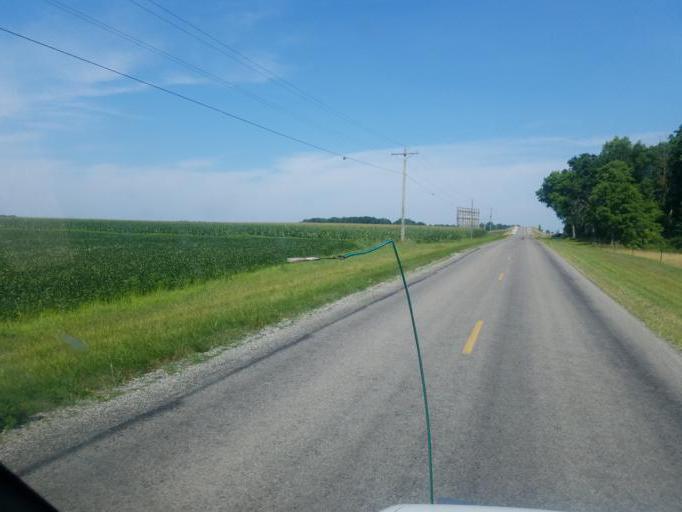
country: US
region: Ohio
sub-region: Shelby County
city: Botkins
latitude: 40.4969
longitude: -84.1749
